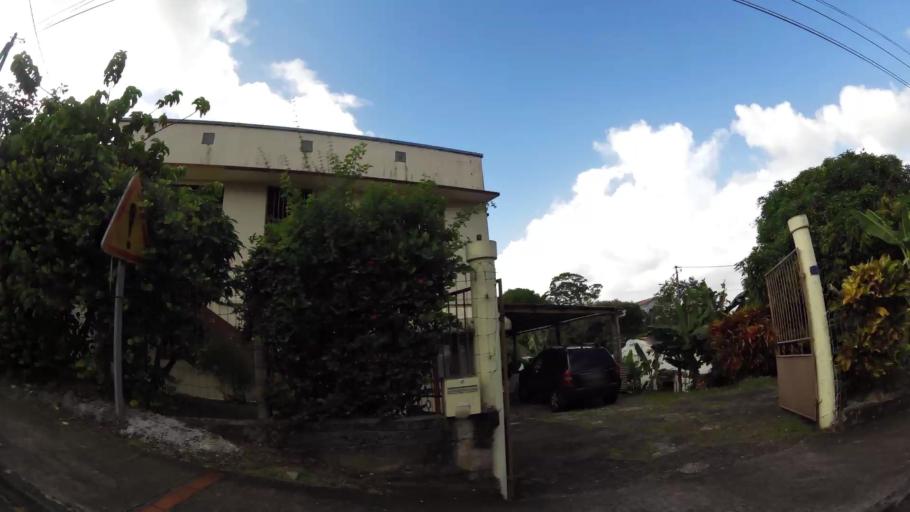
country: MQ
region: Martinique
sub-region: Martinique
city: Ducos
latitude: 14.5764
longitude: -60.9762
